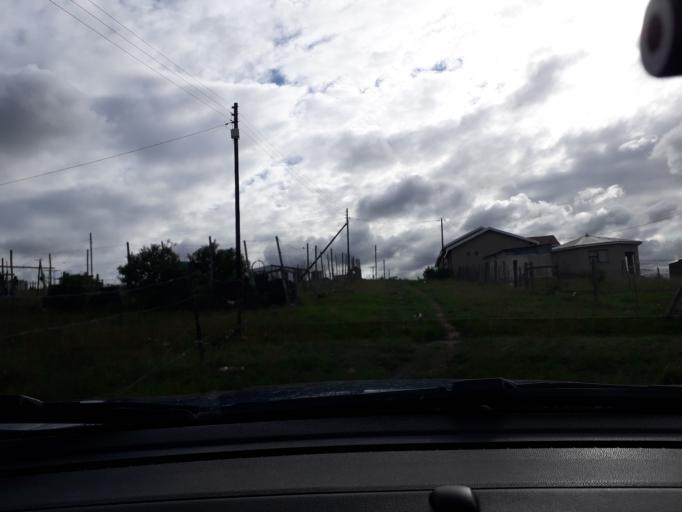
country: ZA
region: Eastern Cape
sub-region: Buffalo City Metropolitan Municipality
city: East London
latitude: -32.8514
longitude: 27.9870
